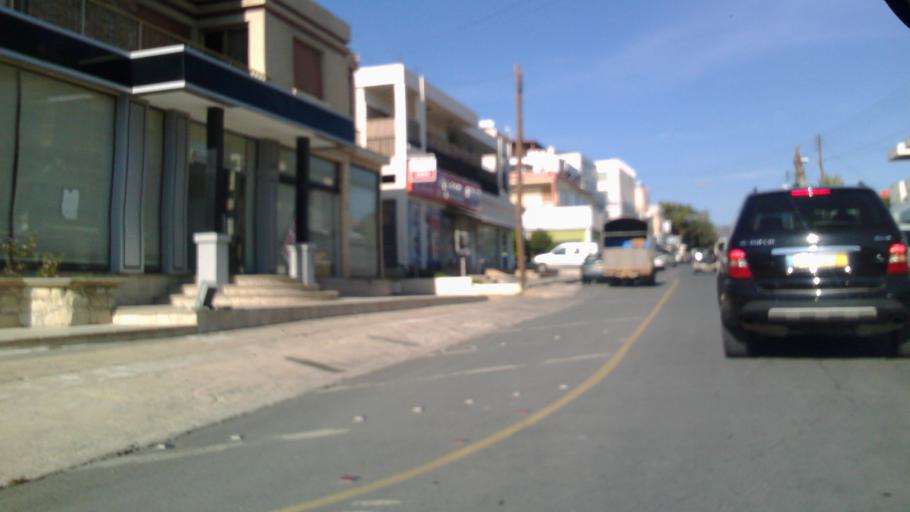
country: CY
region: Pafos
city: Paphos
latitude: 34.7870
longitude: 32.4329
